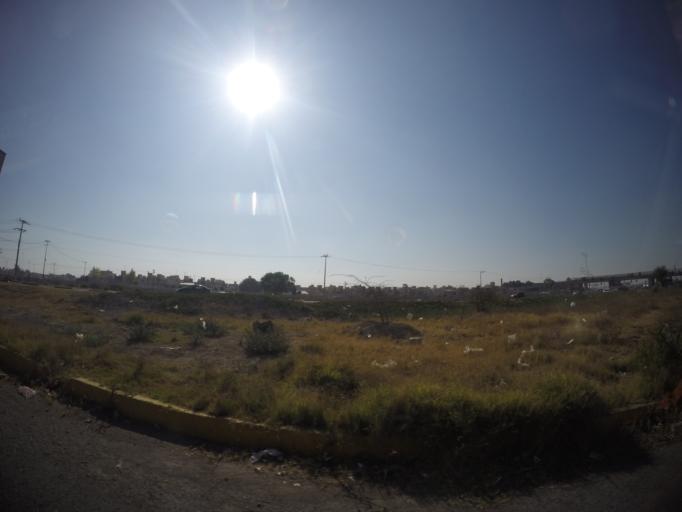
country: MX
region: Mexico
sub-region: Atenco
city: Colonia el Salado
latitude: 19.5901
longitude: -99.0233
